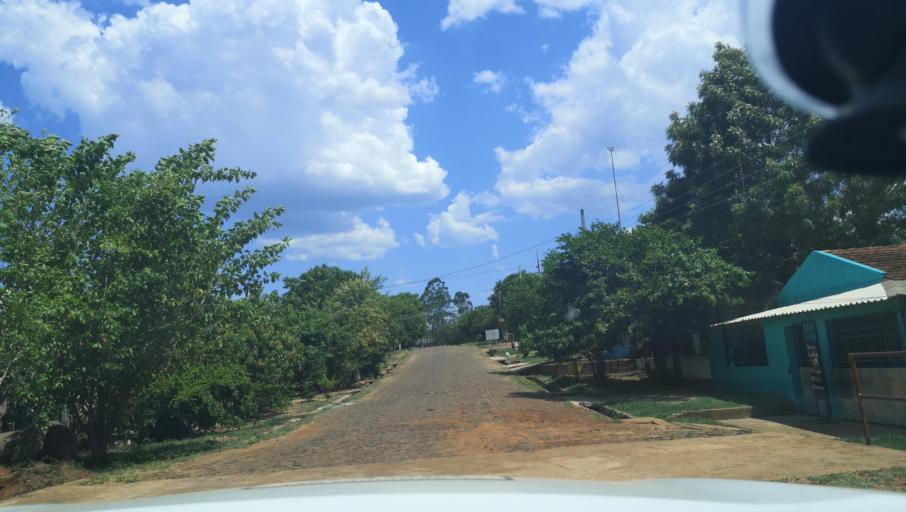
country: PY
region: Itapua
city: Carmen del Parana
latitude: -27.1706
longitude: -56.2450
